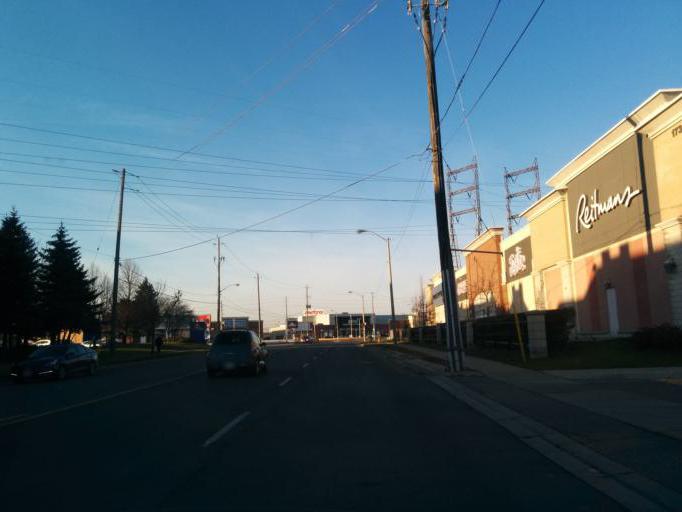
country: CA
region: Ontario
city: Etobicoke
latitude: 43.6168
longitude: -79.5571
